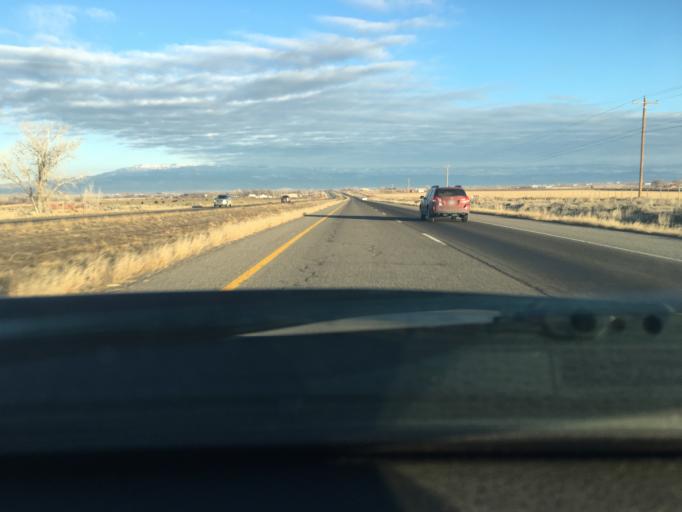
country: US
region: Colorado
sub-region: Montrose County
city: Olathe
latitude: 38.6397
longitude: -107.9876
